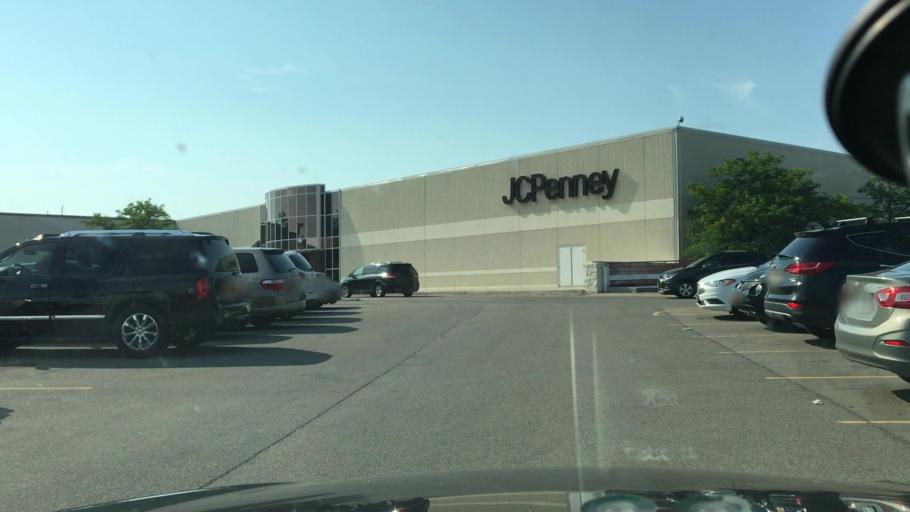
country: US
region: New York
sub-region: Erie County
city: Cheektowaga
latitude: 42.9120
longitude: -78.7616
